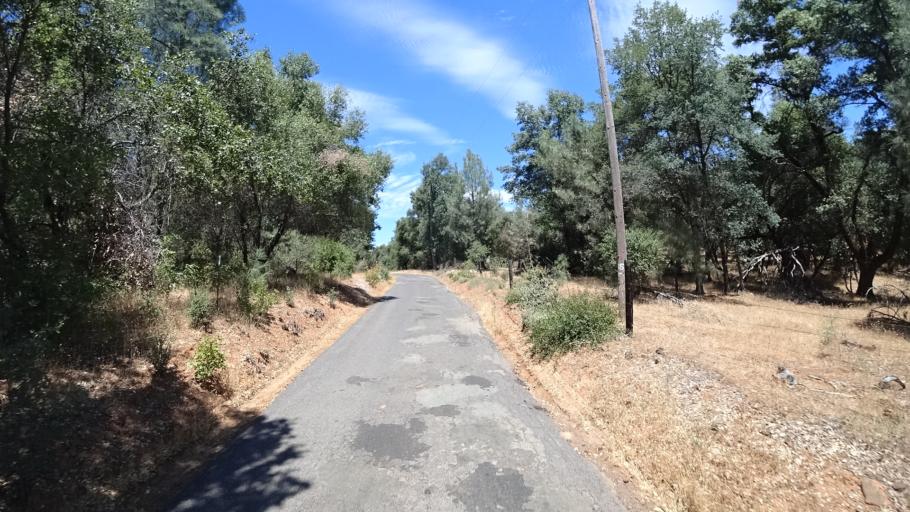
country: US
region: California
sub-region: Calaveras County
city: Forest Meadows
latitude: 38.2240
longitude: -120.4500
